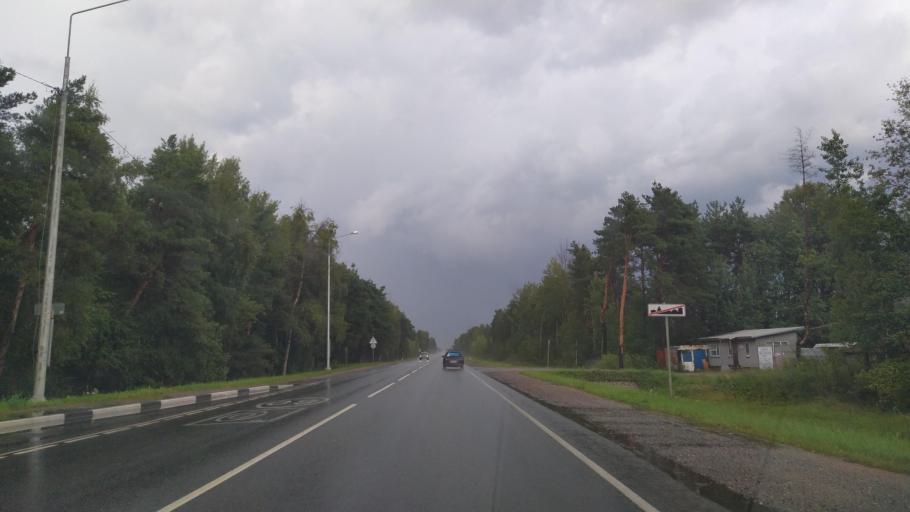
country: RU
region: Pskov
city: Pskov
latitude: 57.7638
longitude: 28.3886
